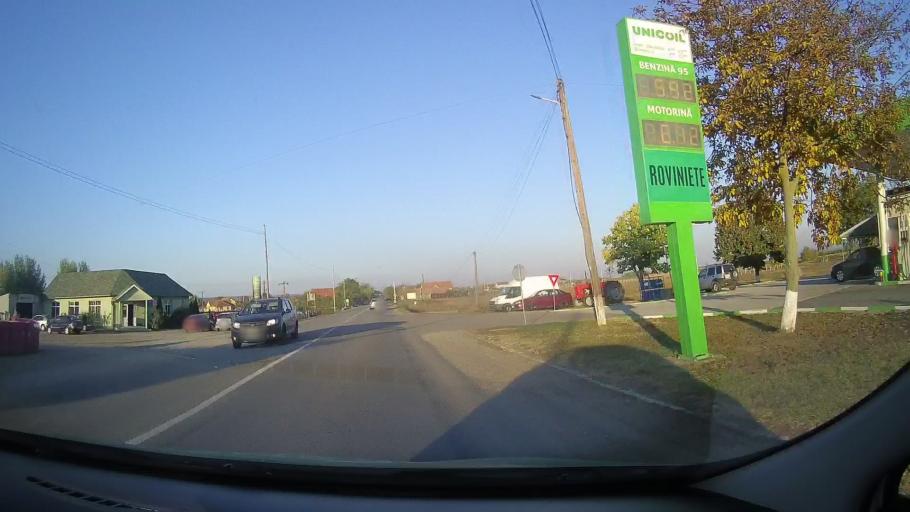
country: RO
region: Bihor
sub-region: Comuna Salard
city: Salard
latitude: 47.2112
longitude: 22.0227
